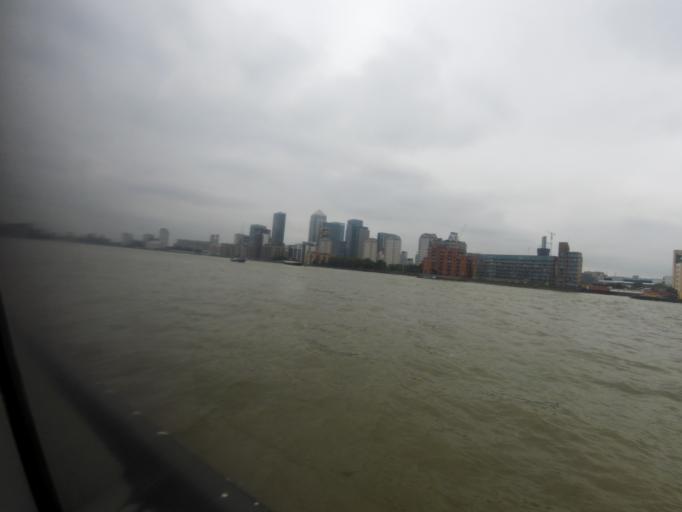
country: GB
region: England
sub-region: Greater London
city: Poplar
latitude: 51.4942
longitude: -0.0314
